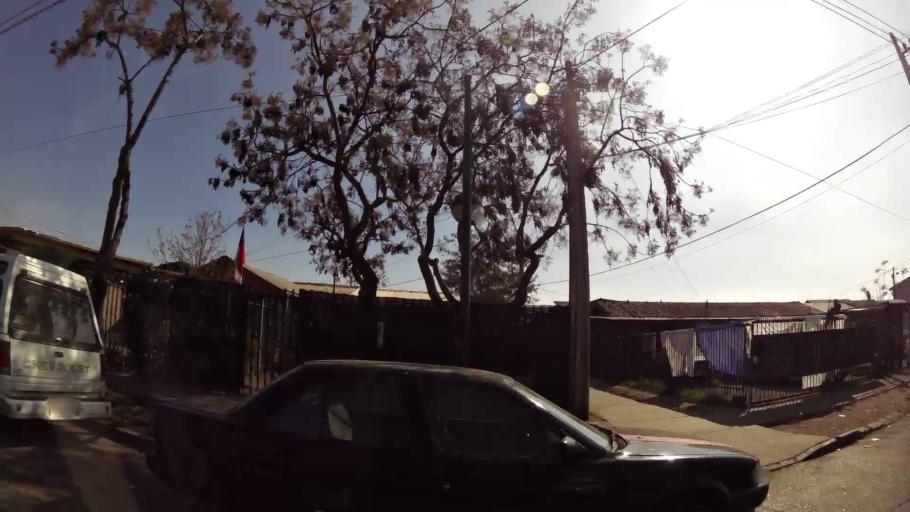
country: CL
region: Santiago Metropolitan
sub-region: Provincia de Santiago
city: Santiago
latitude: -33.4692
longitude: -70.6170
